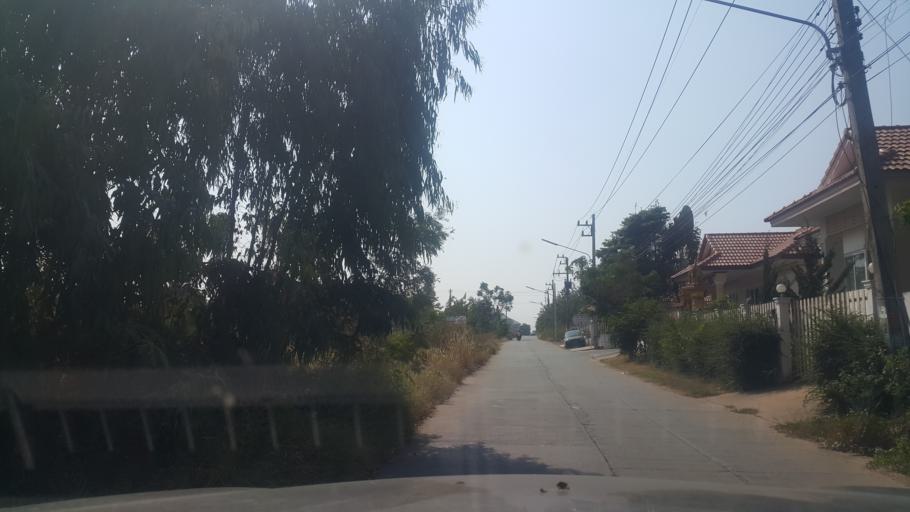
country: TH
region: Nakhon Ratchasima
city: Nakhon Ratchasima
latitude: 14.9334
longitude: 102.0374
